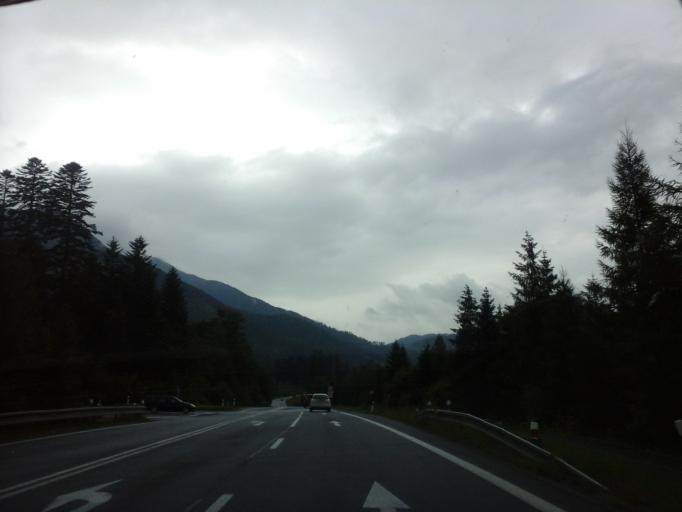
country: SK
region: Presovsky
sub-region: Okres Poprad
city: Zdiar
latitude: 49.2200
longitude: 20.3336
